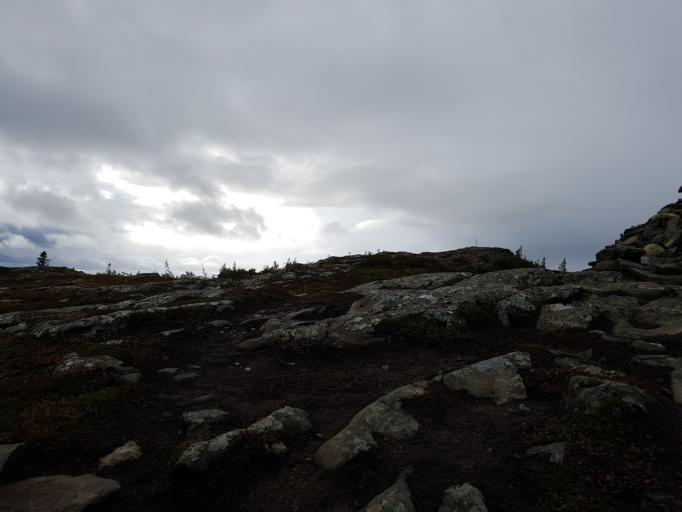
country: NO
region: Sor-Trondelag
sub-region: Melhus
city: Melhus
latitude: 63.4032
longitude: 10.2020
